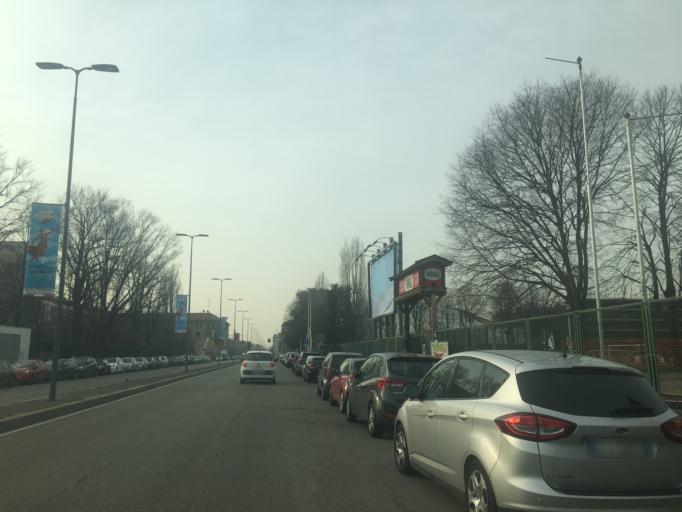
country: IT
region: Lombardy
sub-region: Citta metropolitana di Milano
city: Sesto San Giovanni
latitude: 45.5197
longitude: 9.2109
